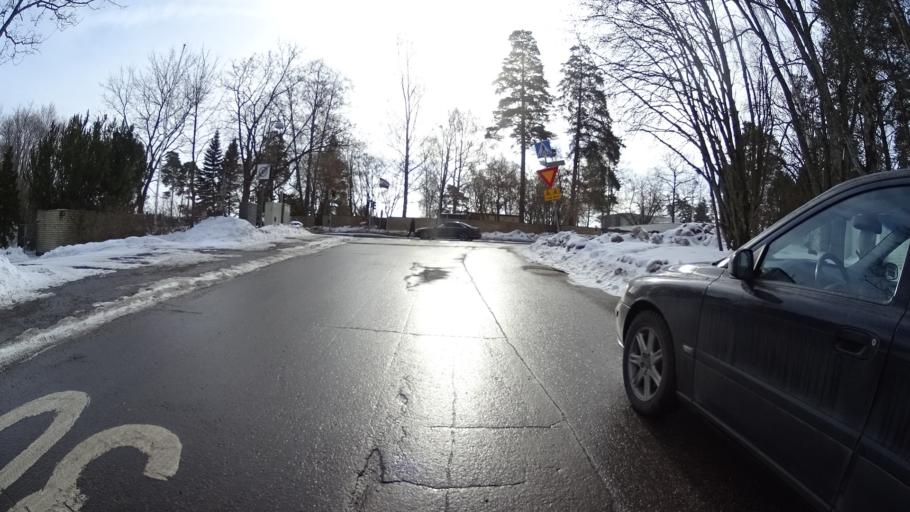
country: FI
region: Uusimaa
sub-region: Helsinki
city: Teekkarikylae
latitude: 60.1874
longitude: 24.8687
